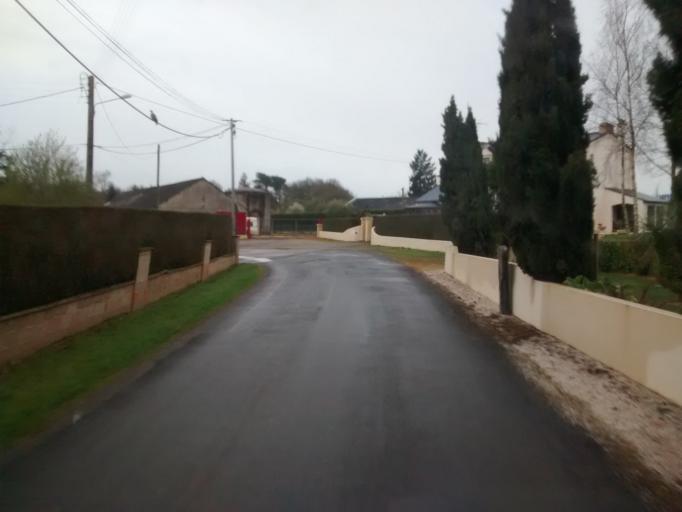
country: FR
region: Brittany
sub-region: Departement du Morbihan
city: Malestroit
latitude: 47.8079
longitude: -2.4022
